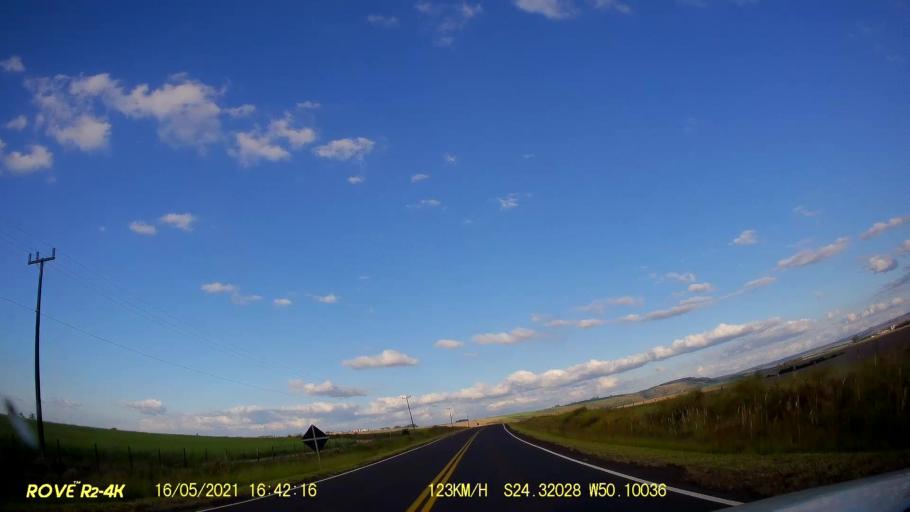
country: BR
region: Parana
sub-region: Pirai Do Sul
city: Pirai do Sul
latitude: -24.3201
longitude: -50.0998
